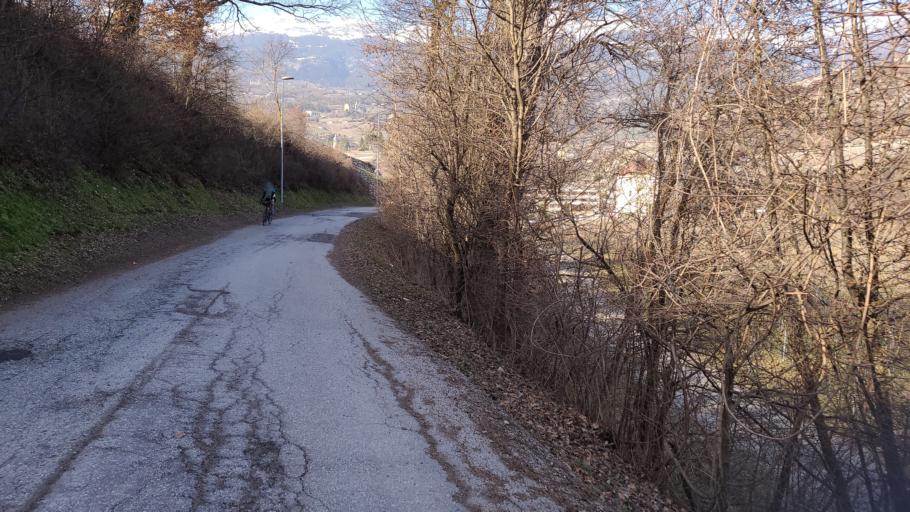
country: CH
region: Valais
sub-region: Sierre District
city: Sierre
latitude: 46.2949
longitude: 7.5448
